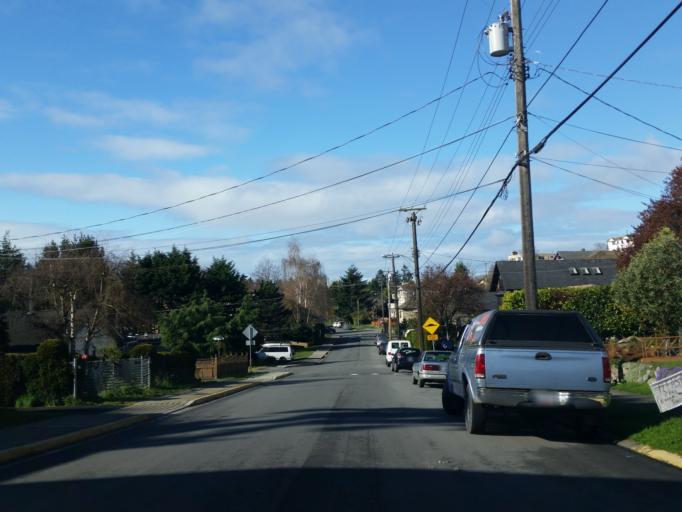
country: CA
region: British Columbia
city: Victoria
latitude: 48.4299
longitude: -123.3974
